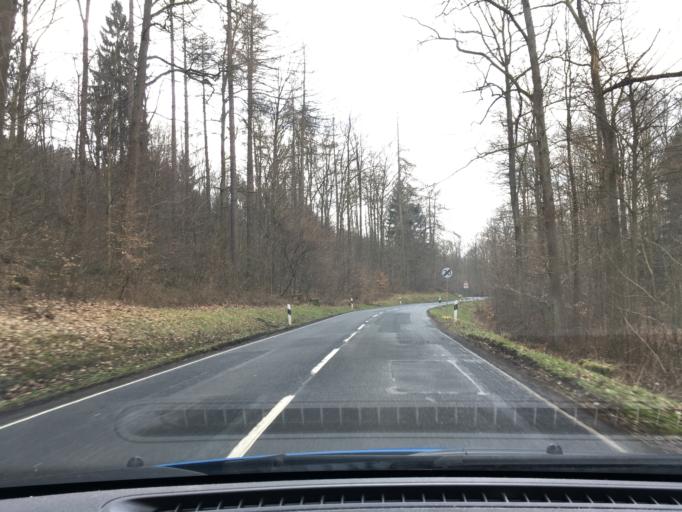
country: DE
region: Lower Saxony
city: Buhren
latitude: 51.5212
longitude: 9.6124
